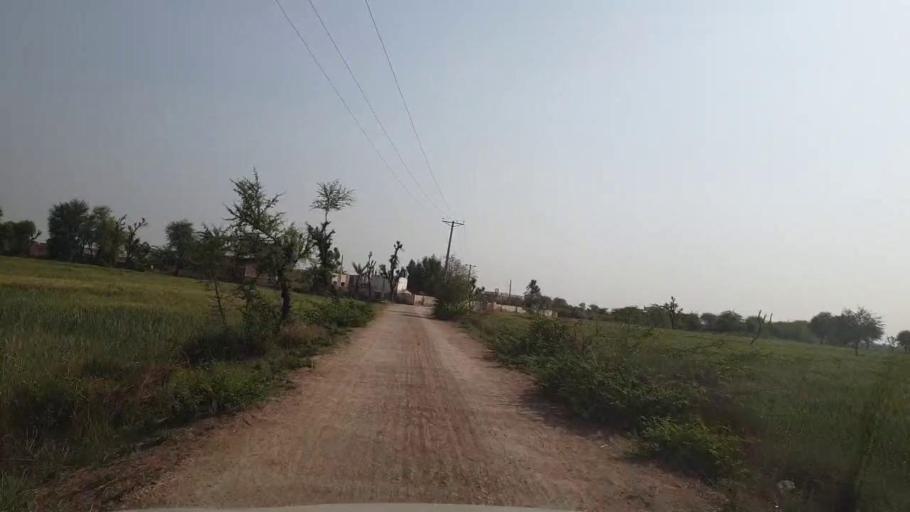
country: PK
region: Sindh
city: Dhoro Naro
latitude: 25.4735
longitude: 69.6467
